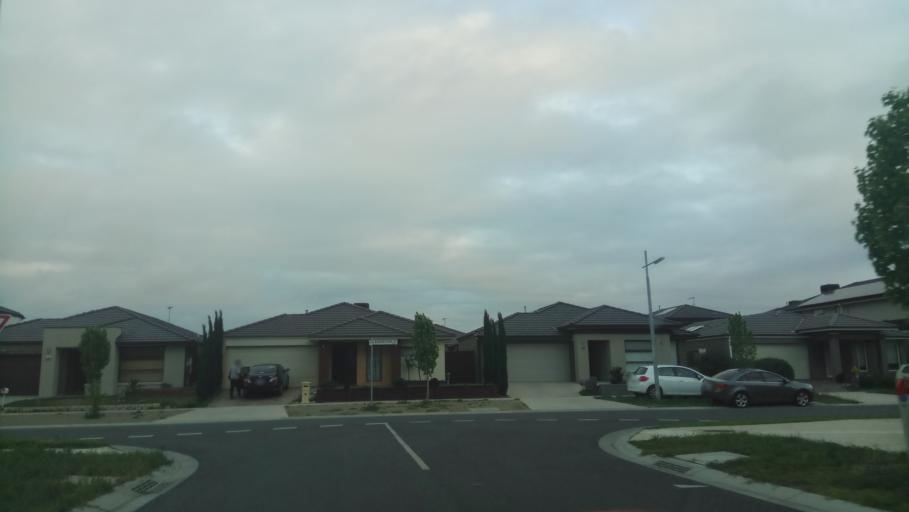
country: AU
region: Victoria
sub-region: Wyndham
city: Point Cook
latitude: -37.9089
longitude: 144.7600
